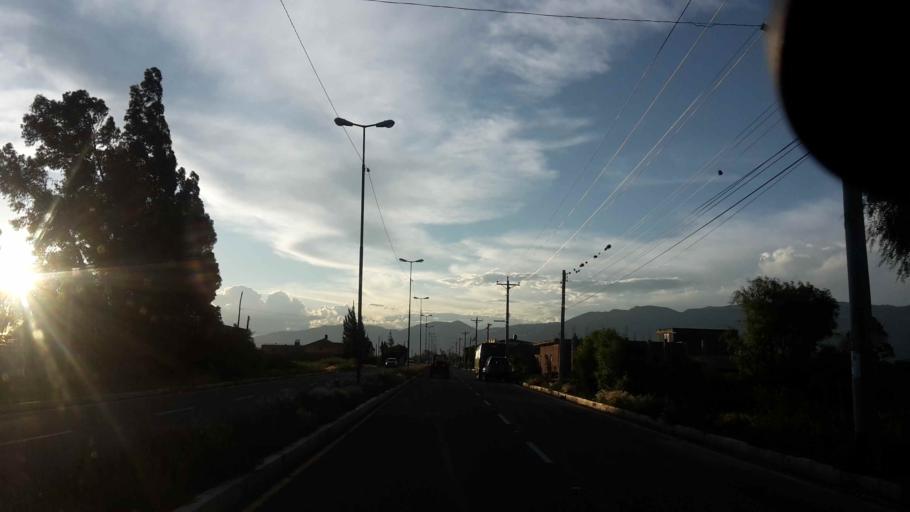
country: BO
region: Cochabamba
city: Punata
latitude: -17.5566
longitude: -65.8089
